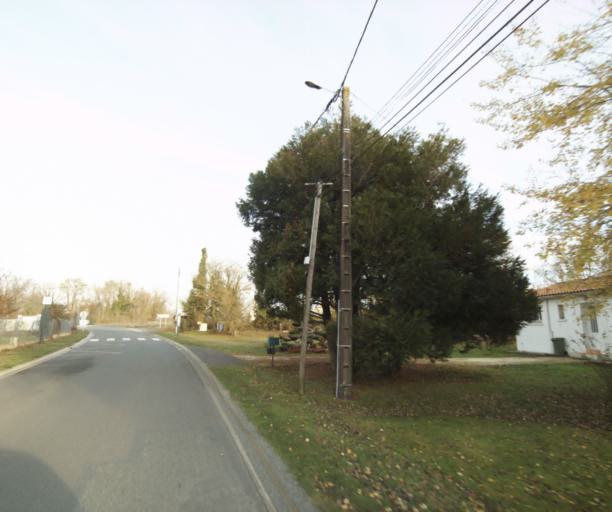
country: FR
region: Poitou-Charentes
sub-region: Departement de la Charente-Maritime
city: Saintes
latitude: 45.7568
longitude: -0.6627
